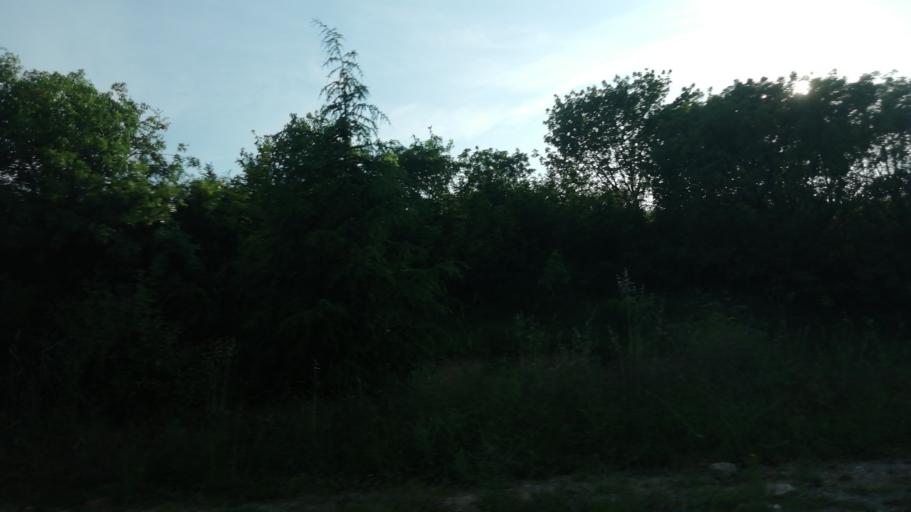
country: TR
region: Karabuk
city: Karabuk
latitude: 41.1293
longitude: 32.6216
